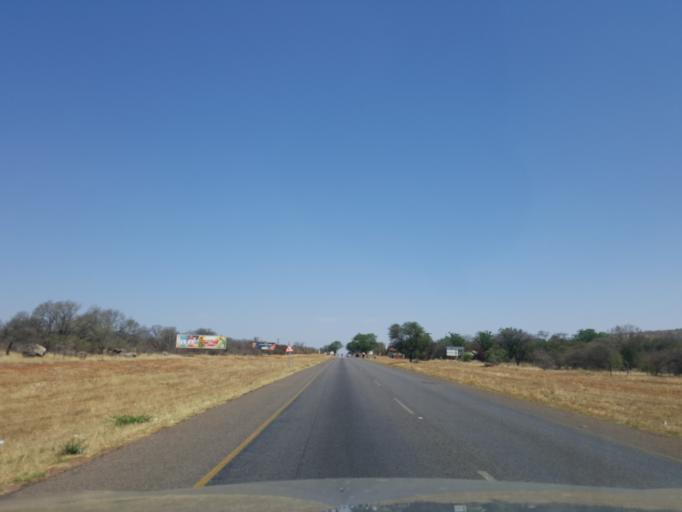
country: BW
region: South East
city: Lobatse
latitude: -25.1674
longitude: 25.6870
